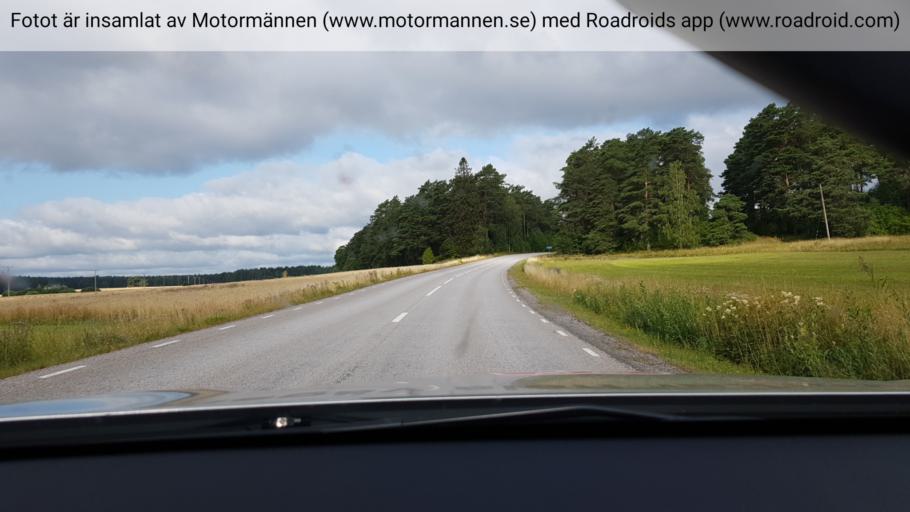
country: SE
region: Stockholm
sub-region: Norrtalje Kommun
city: Nykvarn
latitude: 59.8981
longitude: 18.3505
